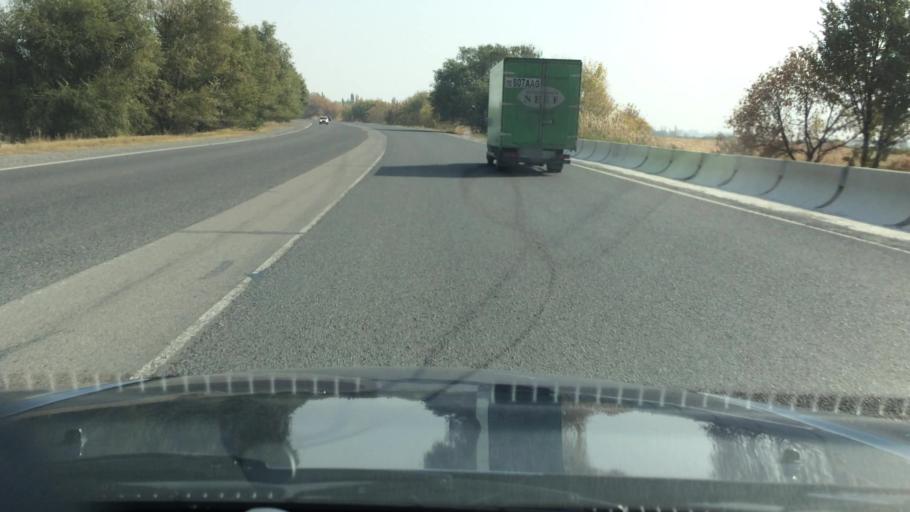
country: KG
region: Chuy
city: Ivanovka
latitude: 42.9401
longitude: 74.9708
